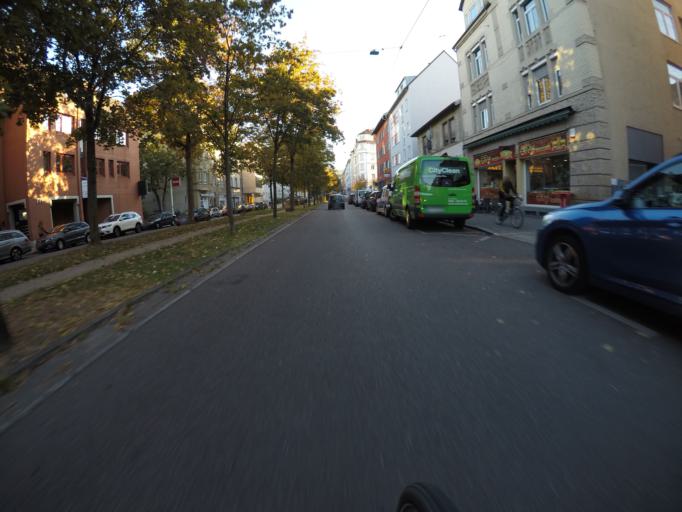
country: DE
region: Baden-Wuerttemberg
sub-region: Regierungsbezirk Stuttgart
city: Stuttgart-Ost
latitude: 48.7848
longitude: 9.2078
